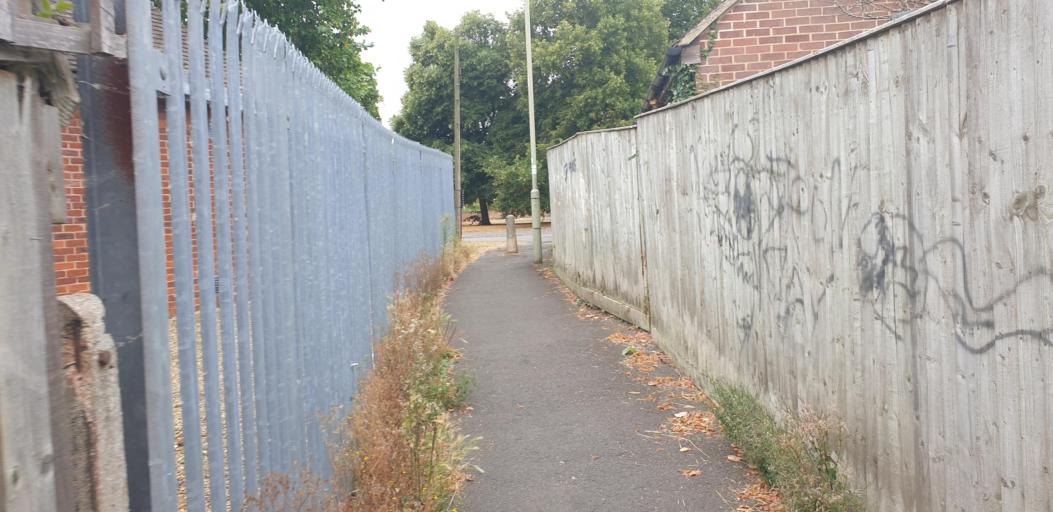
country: GB
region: England
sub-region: Oxfordshire
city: Abingdon
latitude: 51.6792
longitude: -1.2754
